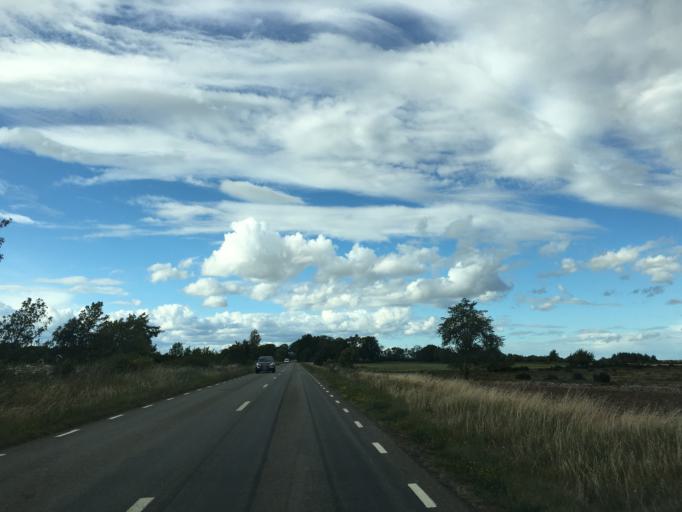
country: SE
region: Kalmar
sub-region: Morbylanga Kommun
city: Moerbylanga
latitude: 56.4110
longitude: 16.4354
